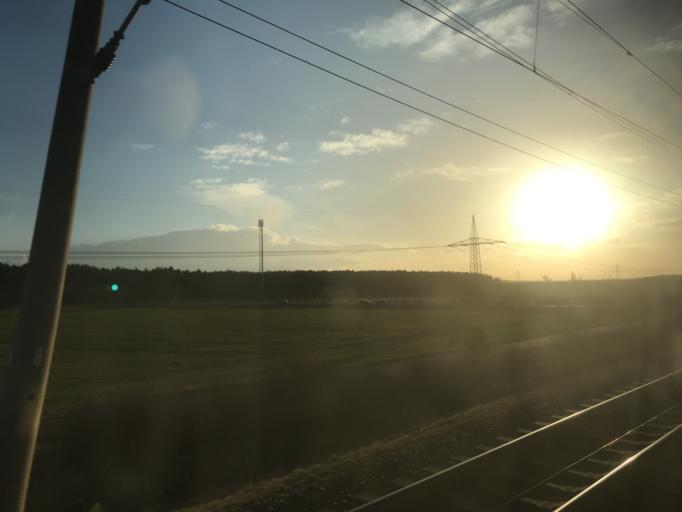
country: DE
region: Saxony-Anhalt
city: Stendal
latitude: 52.5761
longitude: 11.8794
